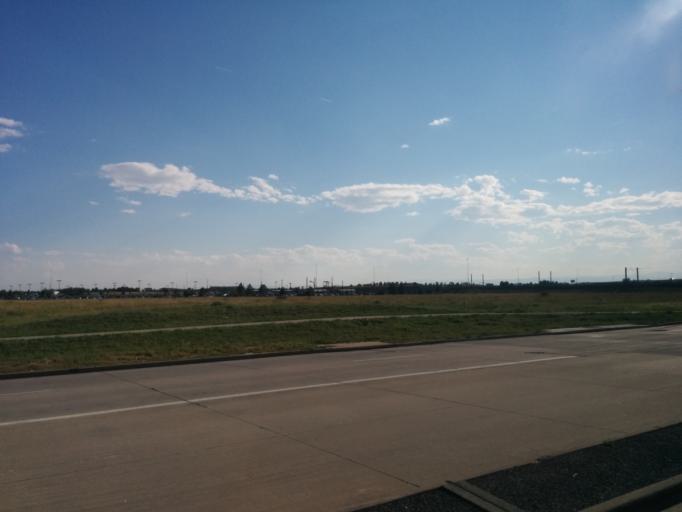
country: US
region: Colorado
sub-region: Adams County
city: Aurora
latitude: 39.7729
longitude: -104.7843
